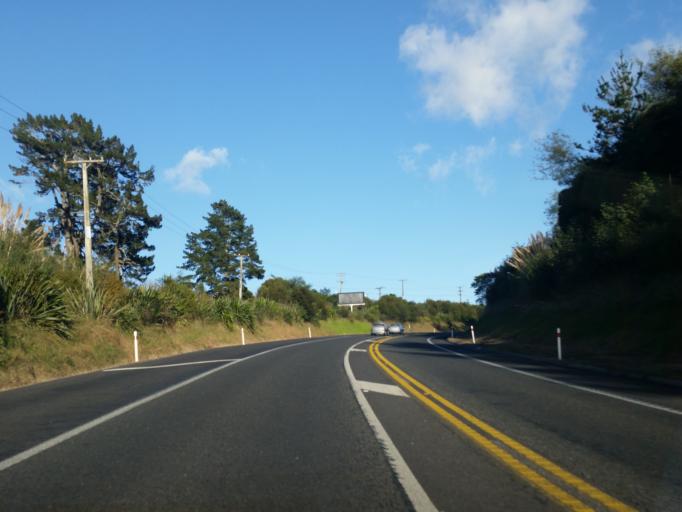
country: NZ
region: Bay of Plenty
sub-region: Tauranga City
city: Tauranga
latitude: -37.7018
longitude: 176.0870
